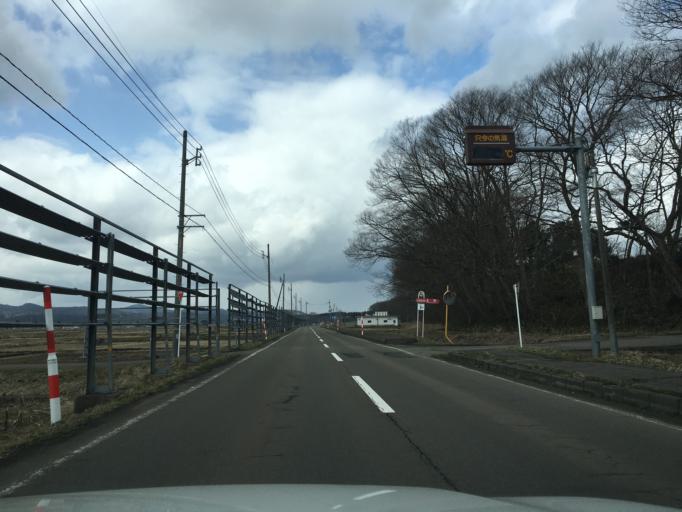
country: JP
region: Akita
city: Takanosu
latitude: 40.1465
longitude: 140.3436
